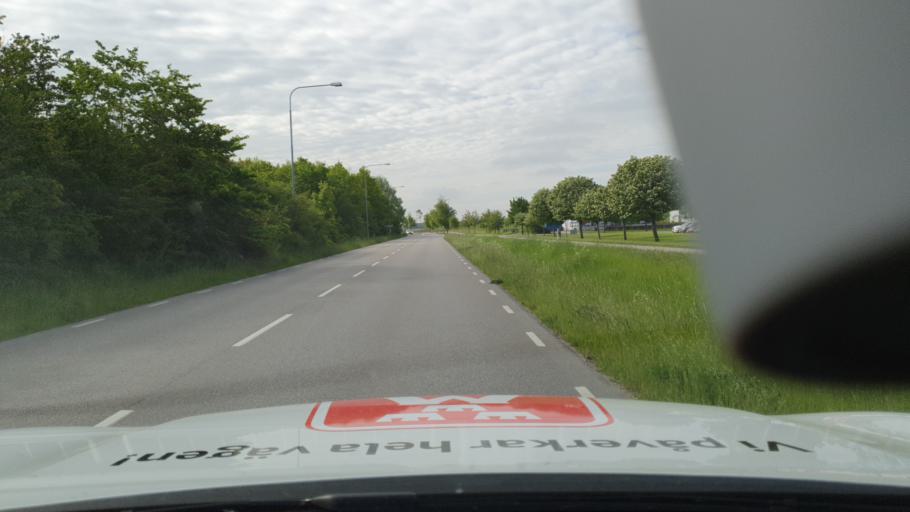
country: SE
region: Skane
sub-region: Vellinge Kommun
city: Vellinge
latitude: 55.4622
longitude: 13.0197
